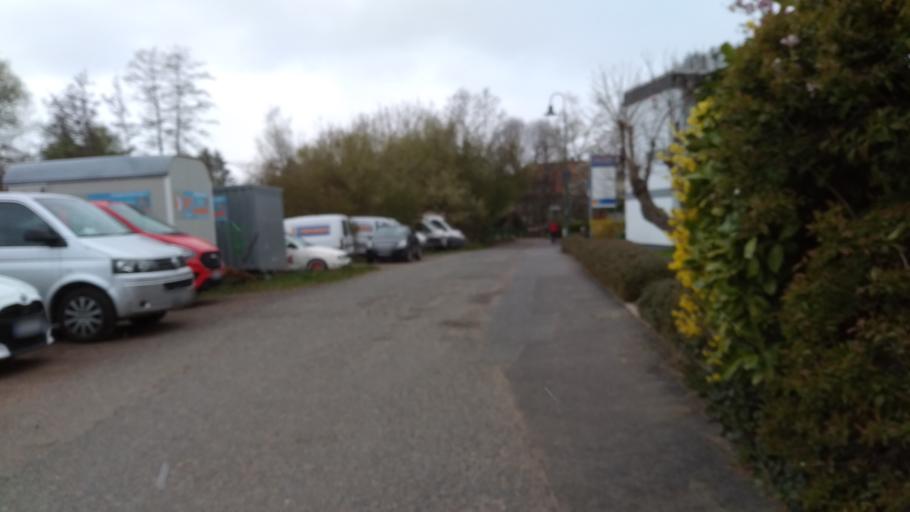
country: DE
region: Hesse
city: Pfungstadt
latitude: 49.8141
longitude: 8.6423
